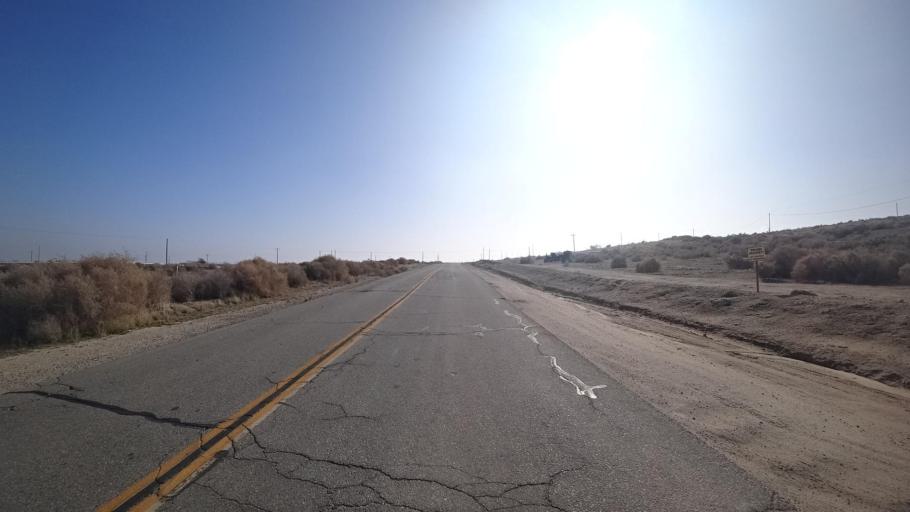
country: US
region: California
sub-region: Kern County
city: Taft Heights
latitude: 35.1669
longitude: -119.5325
